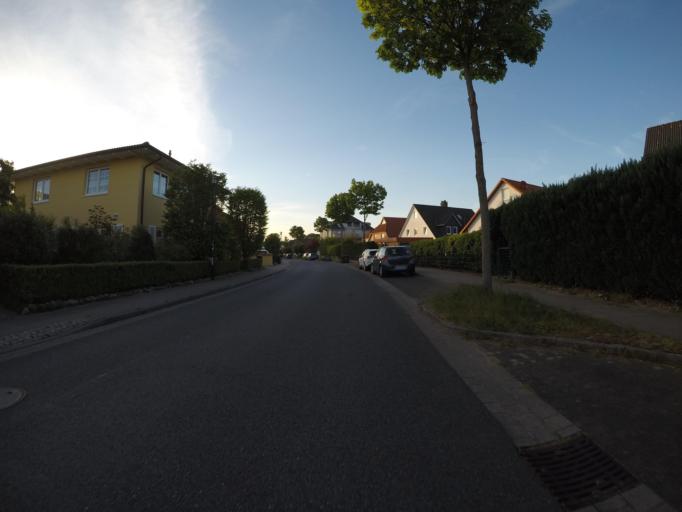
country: DE
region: Lower Saxony
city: Lueneburg
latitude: 53.2394
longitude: 10.3839
